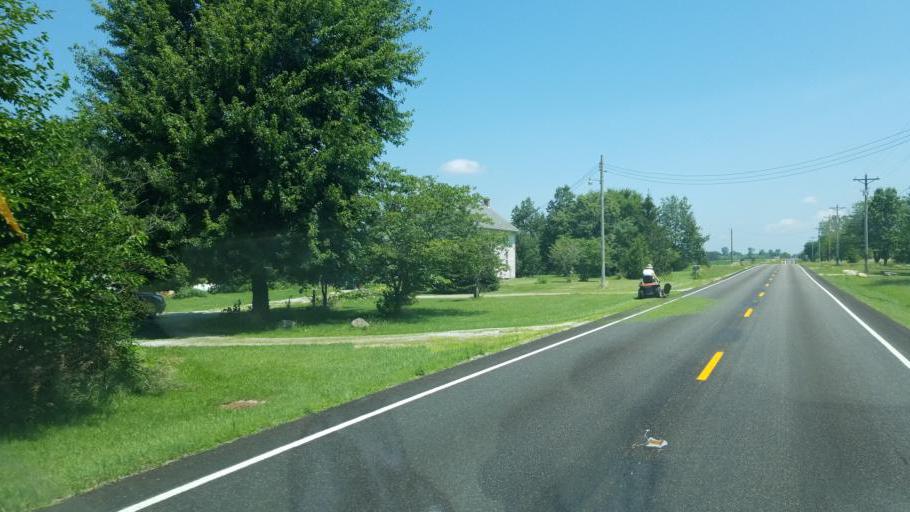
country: US
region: Ohio
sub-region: Sandusky County
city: Green Springs
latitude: 41.2324
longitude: -83.0168
